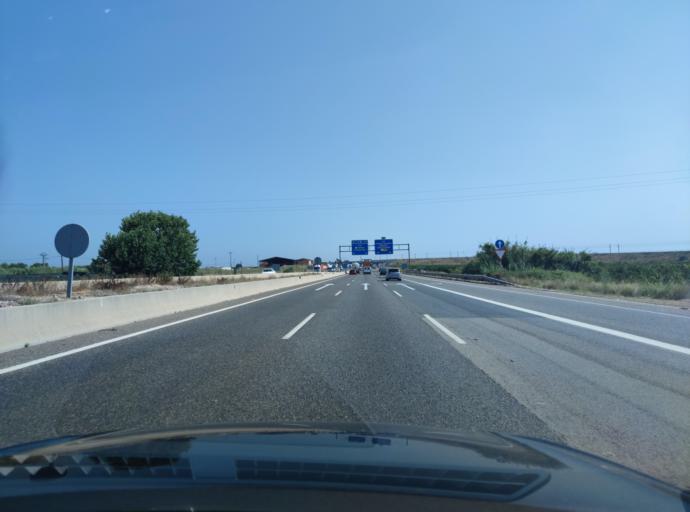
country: ES
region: Valencia
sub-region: Provincia de Valencia
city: Silla
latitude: 39.3354
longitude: -0.4316
